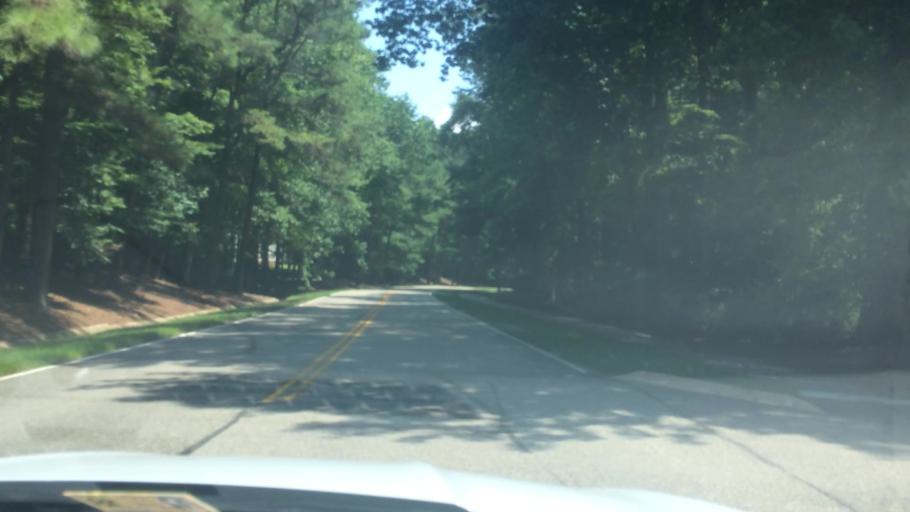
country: US
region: Virginia
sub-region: City of Williamsburg
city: Williamsburg
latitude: 37.2453
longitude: -76.6688
